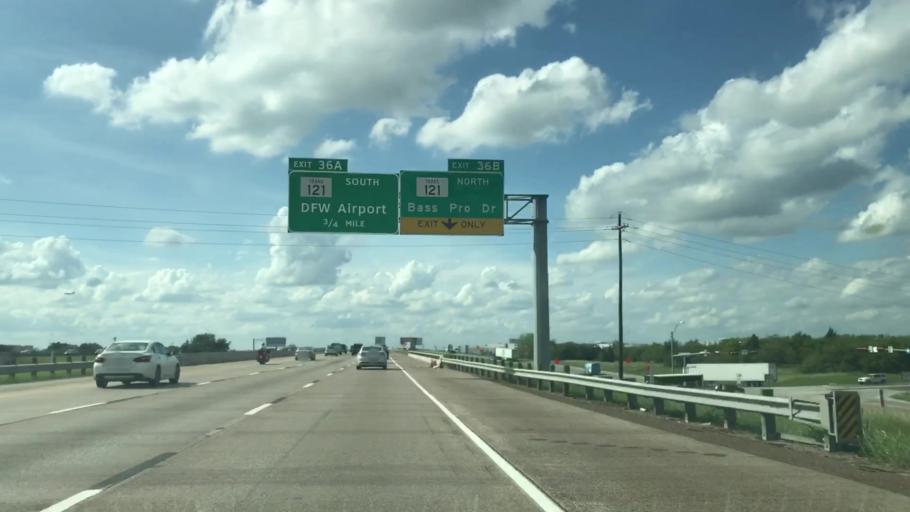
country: US
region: Texas
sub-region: Dallas County
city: Coppell
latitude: 32.9456
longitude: -97.0213
